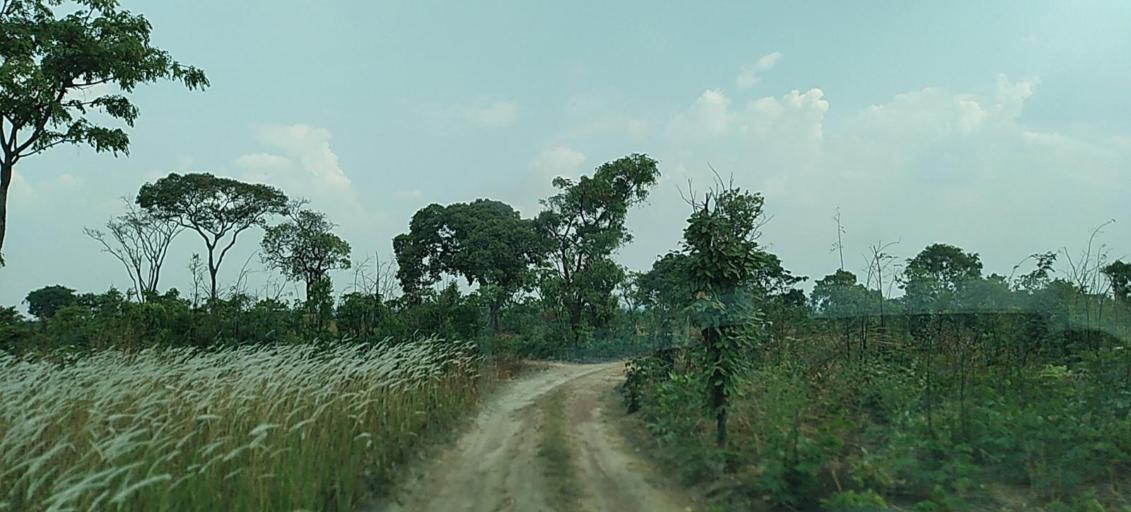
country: ZM
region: North-Western
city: Solwezi
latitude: -12.0969
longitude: 26.2847
